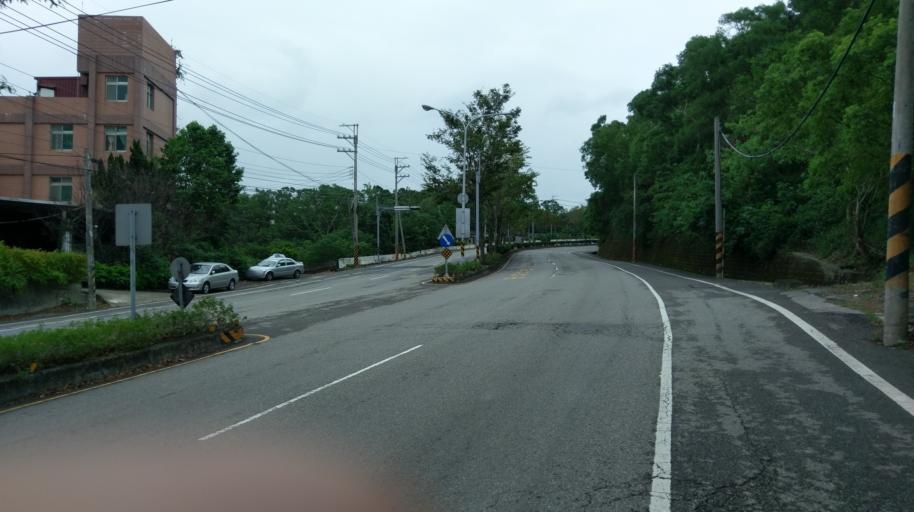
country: TW
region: Taiwan
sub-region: Miaoli
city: Miaoli
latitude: 24.6462
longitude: 120.8455
